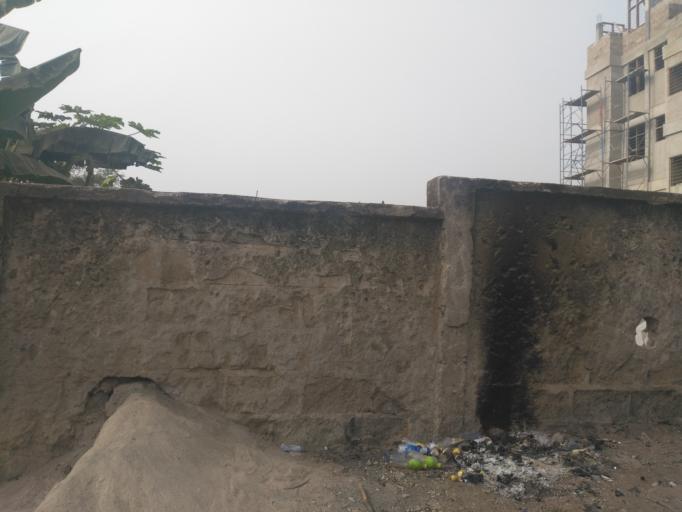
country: GH
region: Ashanti
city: Kumasi
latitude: 6.6981
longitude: -1.6332
